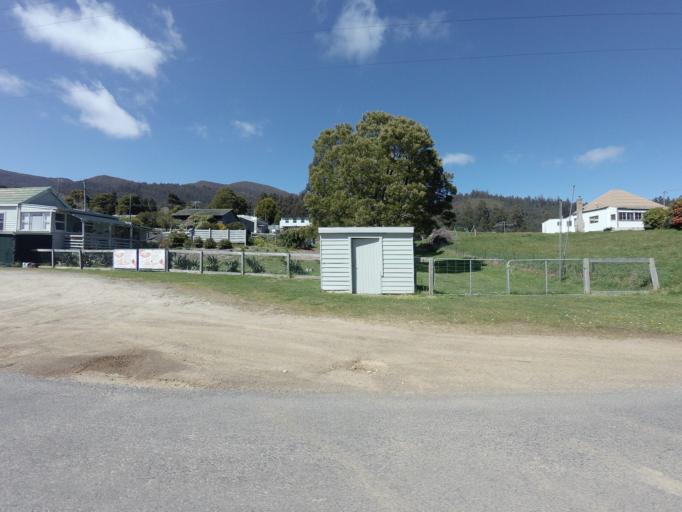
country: AU
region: Tasmania
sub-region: Derwent Valley
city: New Norfolk
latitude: -42.7562
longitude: 146.6235
